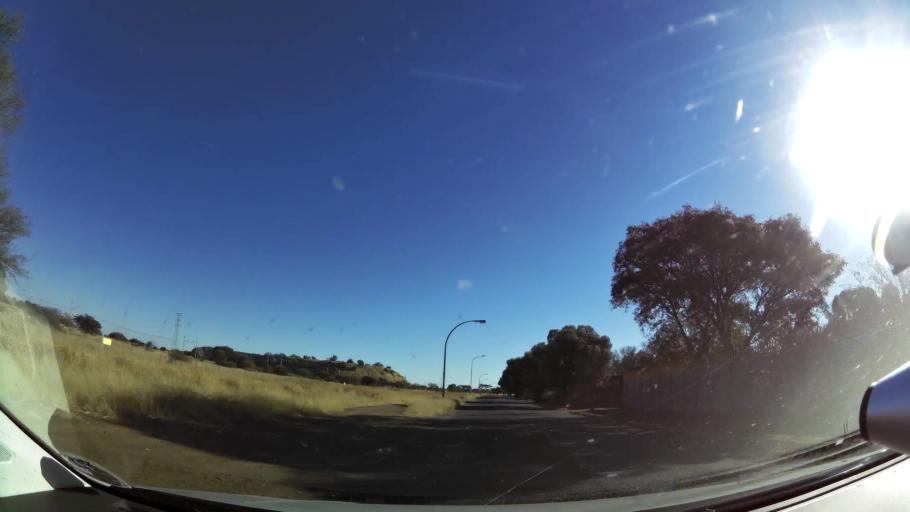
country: ZA
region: Northern Cape
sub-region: Frances Baard District Municipality
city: Kimberley
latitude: -28.7441
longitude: 24.7918
